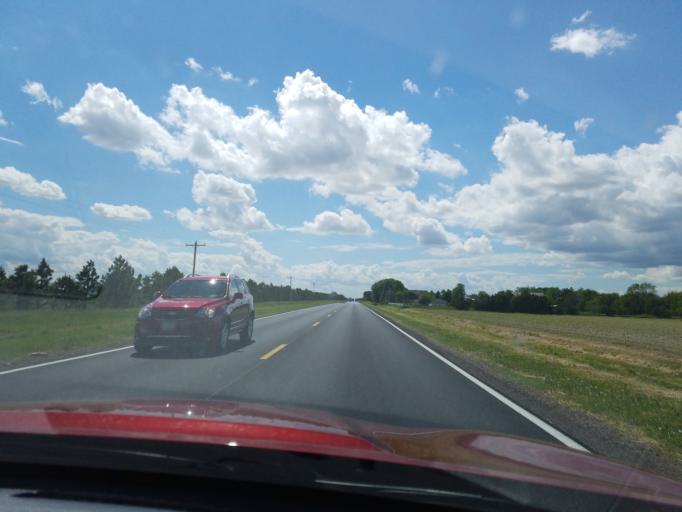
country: US
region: Nebraska
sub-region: Buffalo County
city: Kearney
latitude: 40.6410
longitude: -99.0277
